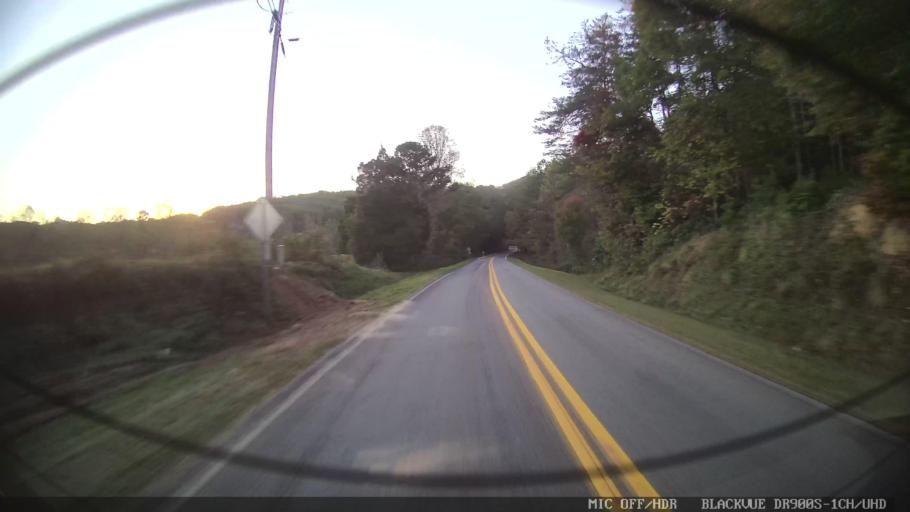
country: US
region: Georgia
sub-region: Union County
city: Blairsville
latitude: 34.8548
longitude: -83.9009
